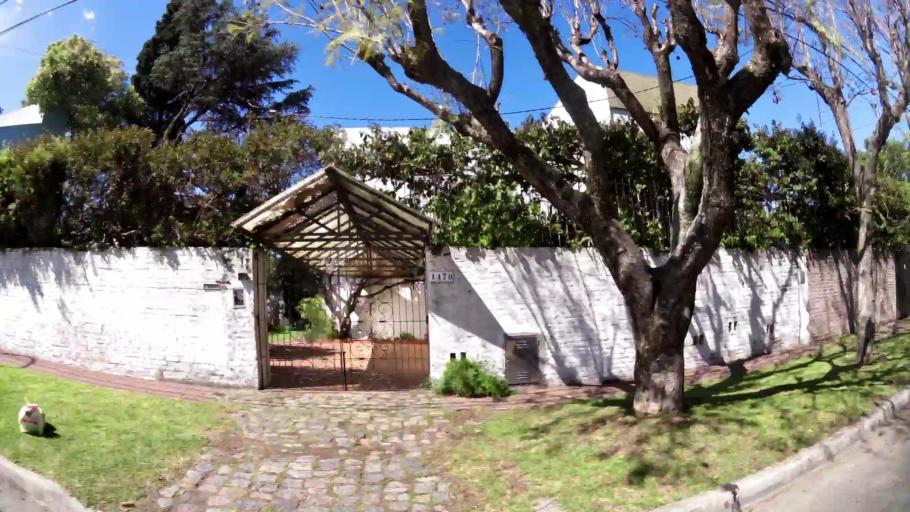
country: AR
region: Buenos Aires
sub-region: Partido de Quilmes
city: Quilmes
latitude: -34.6996
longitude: -58.3032
